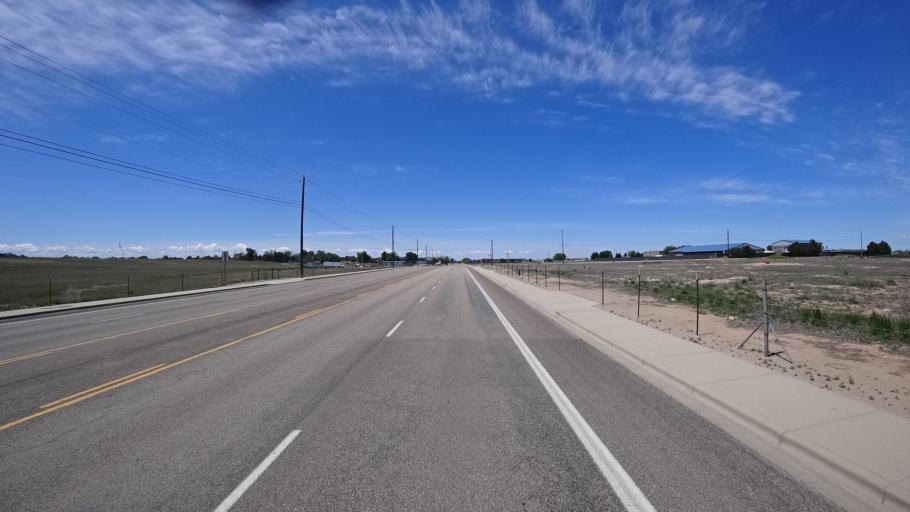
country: US
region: Idaho
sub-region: Ada County
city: Garden City
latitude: 43.5753
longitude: -116.2571
